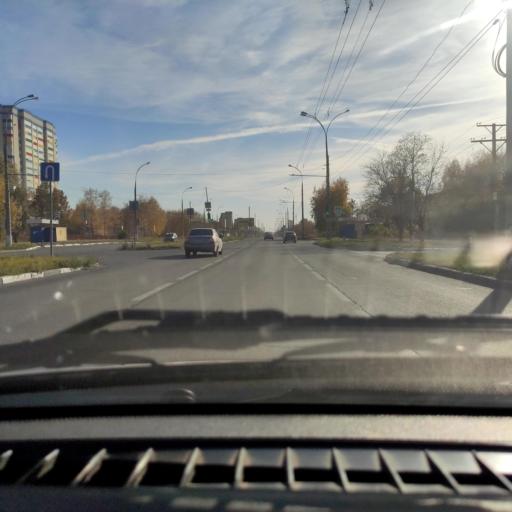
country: RU
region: Samara
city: Tol'yatti
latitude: 53.5437
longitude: 49.3005
